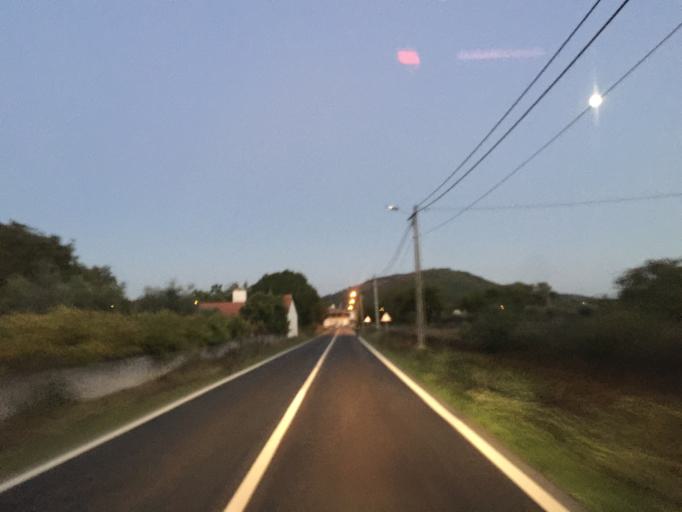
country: PT
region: Portalegre
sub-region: Marvao
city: Marvao
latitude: 39.3868
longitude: -7.4016
